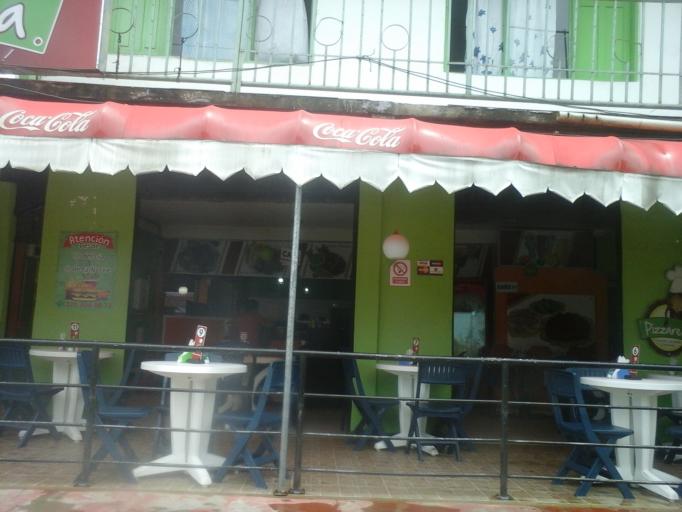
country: CO
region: Putumayo
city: Orito
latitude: 0.6653
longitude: -76.8708
